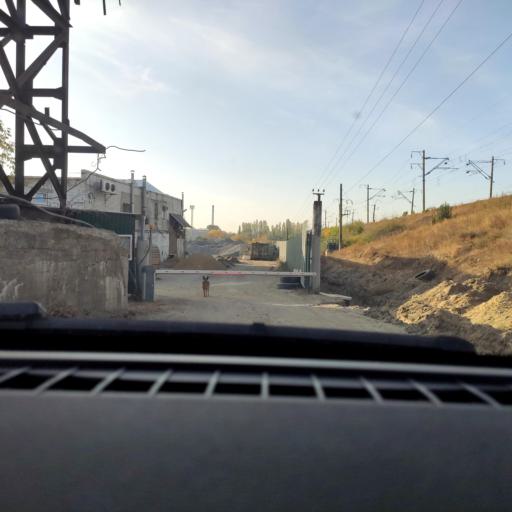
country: RU
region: Voronezj
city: Maslovka
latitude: 51.6247
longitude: 39.2577
